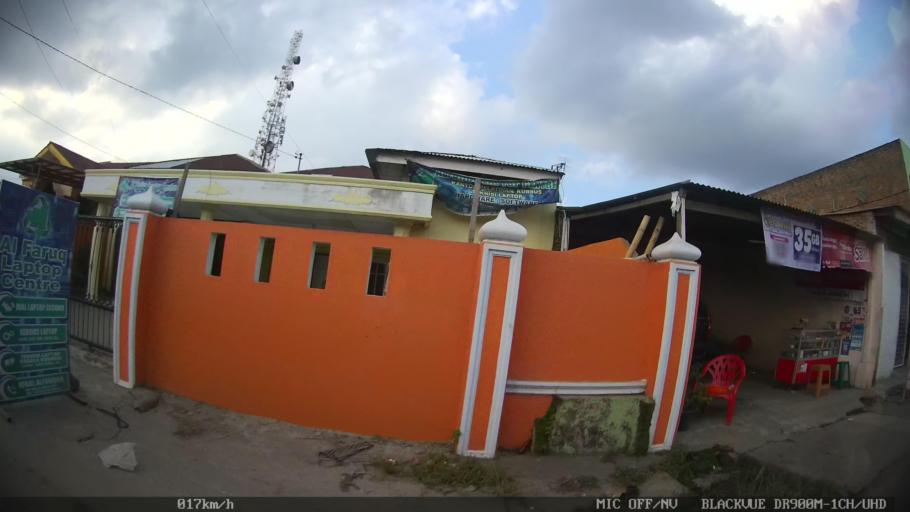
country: ID
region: North Sumatra
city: Medan
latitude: 3.5853
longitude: 98.7399
